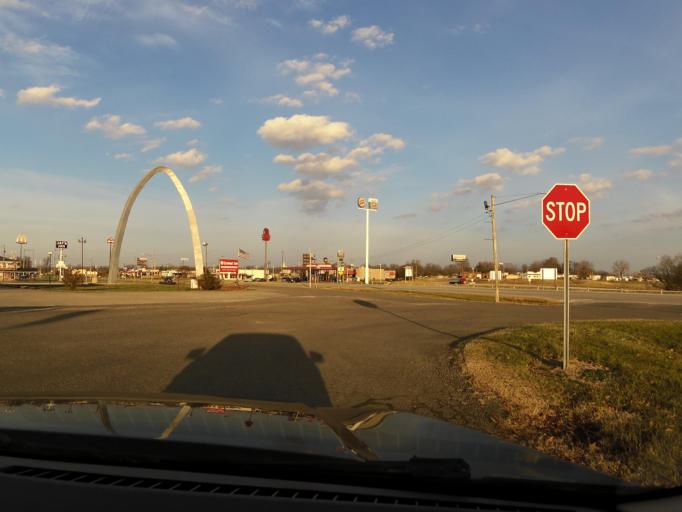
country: US
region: Illinois
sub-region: Fayette County
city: Vandalia
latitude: 38.9764
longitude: -89.0972
